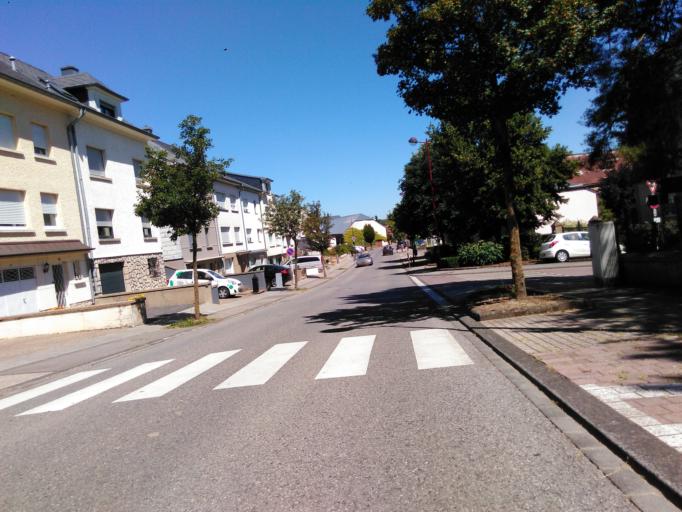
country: LU
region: Luxembourg
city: Bergem
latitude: 49.5082
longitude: 6.0558
